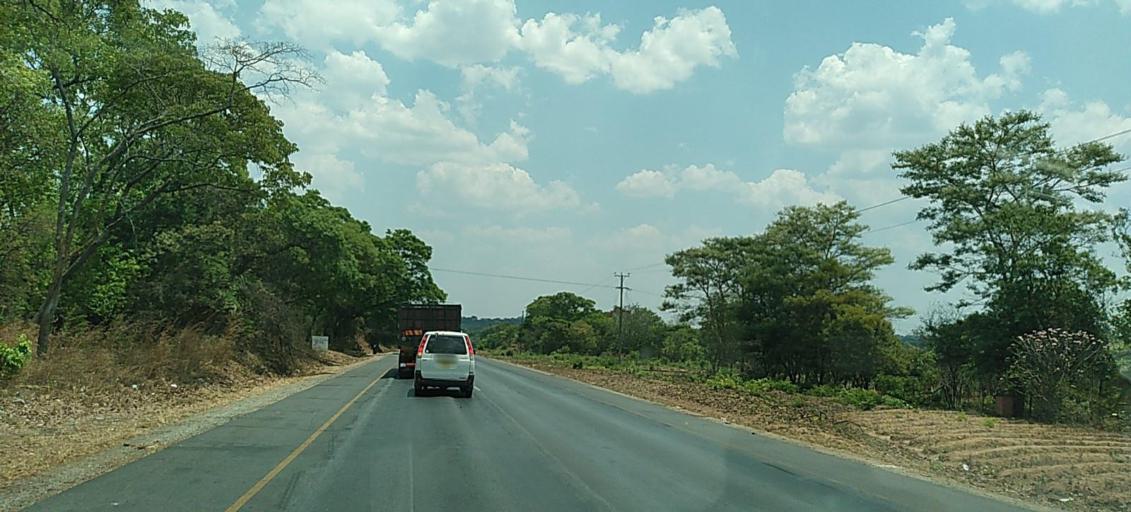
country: ZM
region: Central
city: Kapiri Mposhi
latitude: -14.2061
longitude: 28.5848
